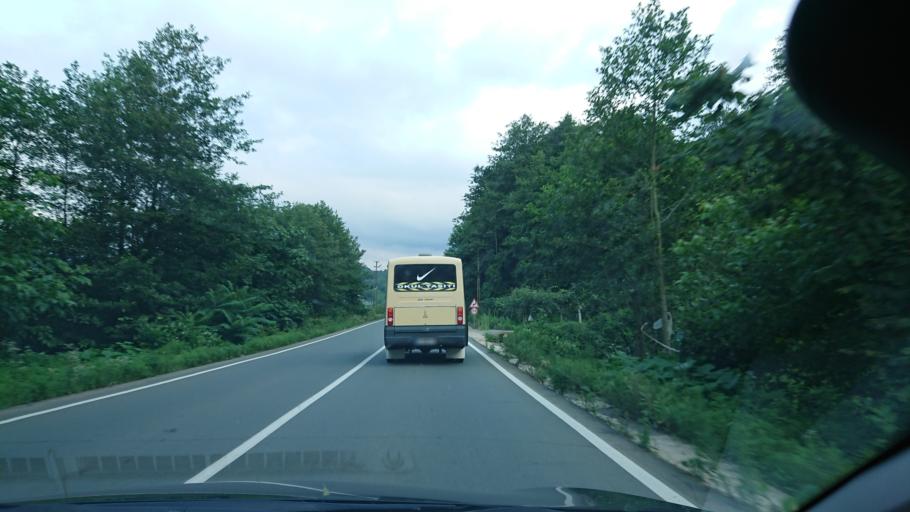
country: TR
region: Rize
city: Cayeli
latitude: 41.0696
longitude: 40.7123
